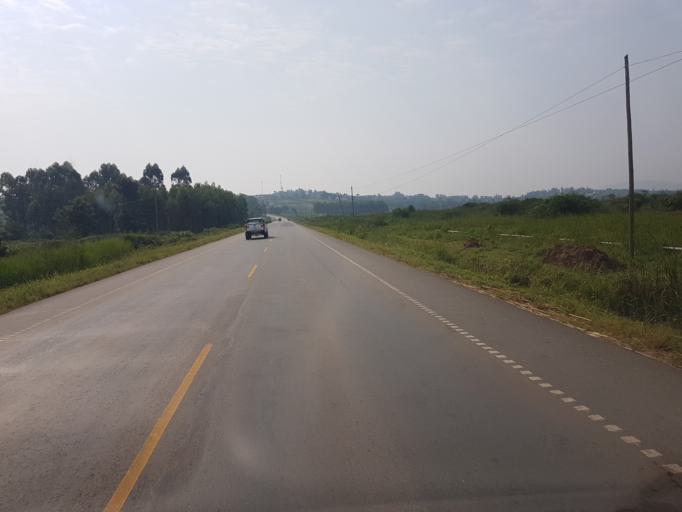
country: UG
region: Western Region
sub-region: Mbarara District
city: Bwizibwera
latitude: -0.6424
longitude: 30.5797
